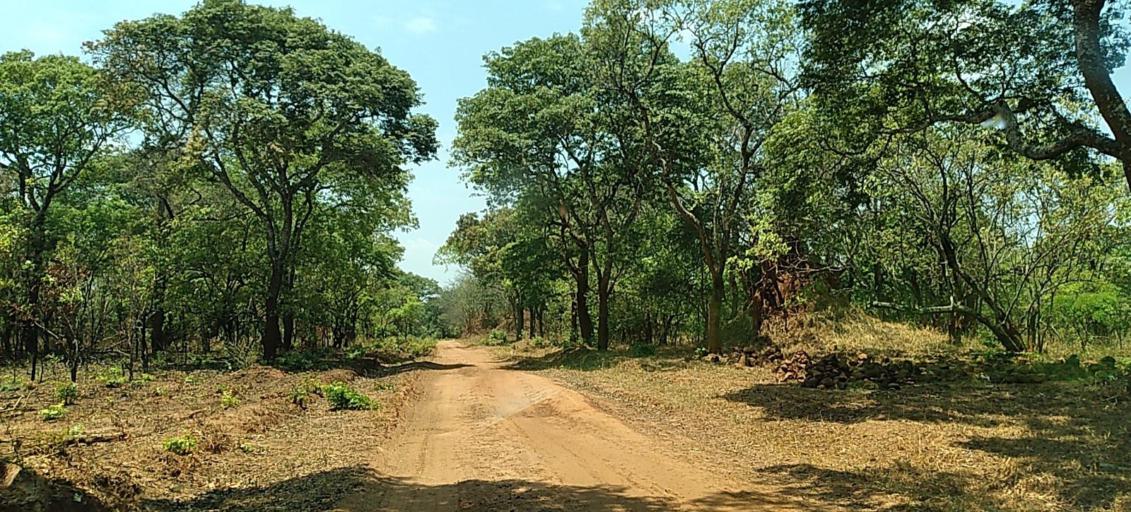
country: CD
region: Katanga
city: Kolwezi
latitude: -11.3559
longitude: 25.2097
